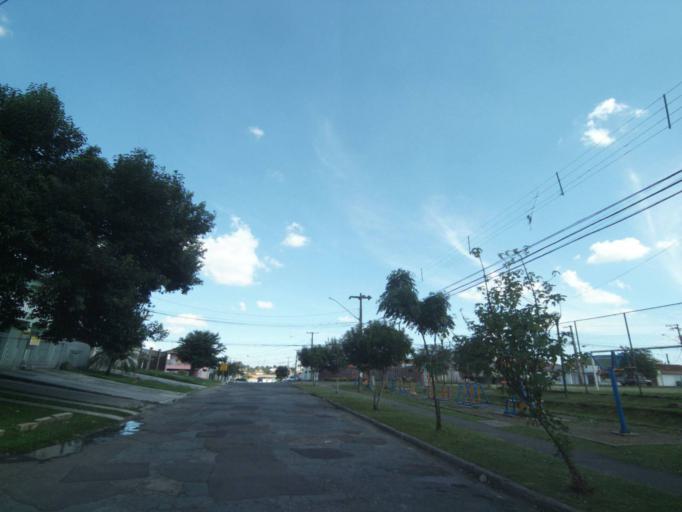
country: BR
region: Parana
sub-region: Pinhais
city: Pinhais
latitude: -25.4623
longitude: -49.2137
